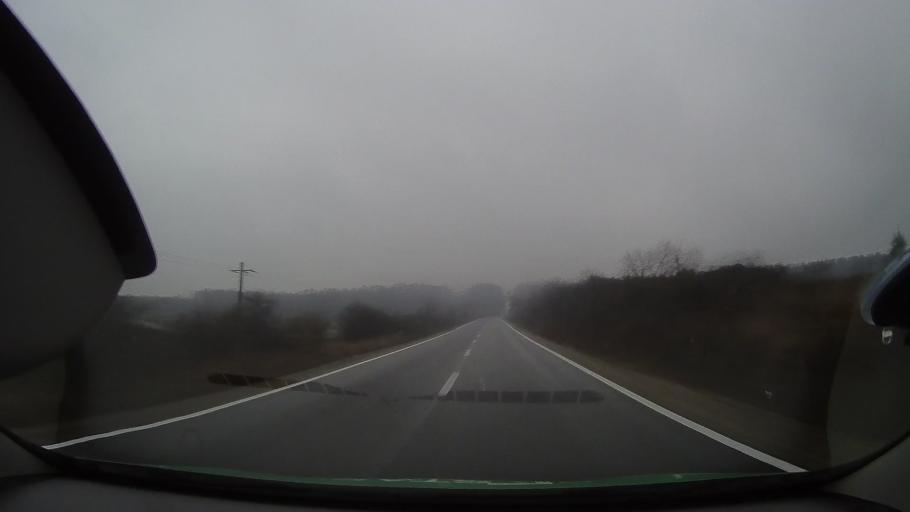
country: RO
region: Bihor
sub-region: Comuna Olcea
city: Olcea
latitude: 46.7055
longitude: 21.9628
